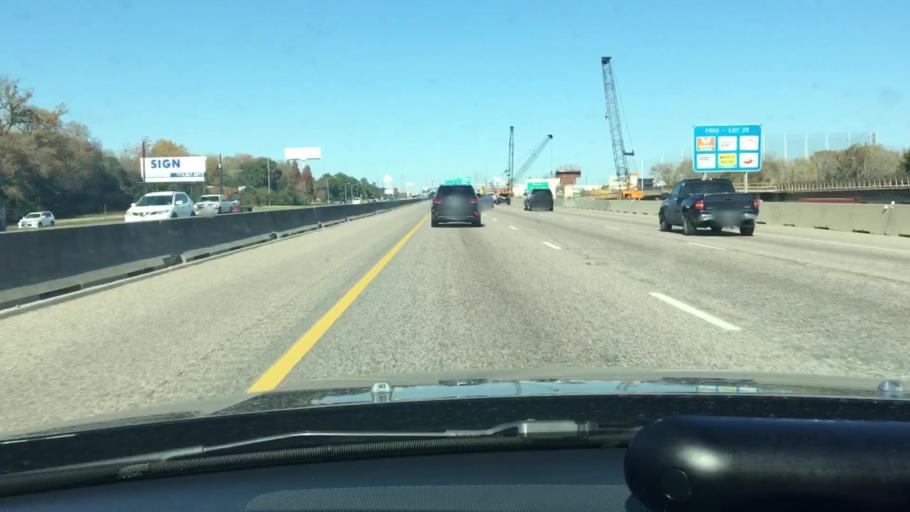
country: US
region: Texas
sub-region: Galveston County
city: League City
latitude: 29.5100
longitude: -95.1181
